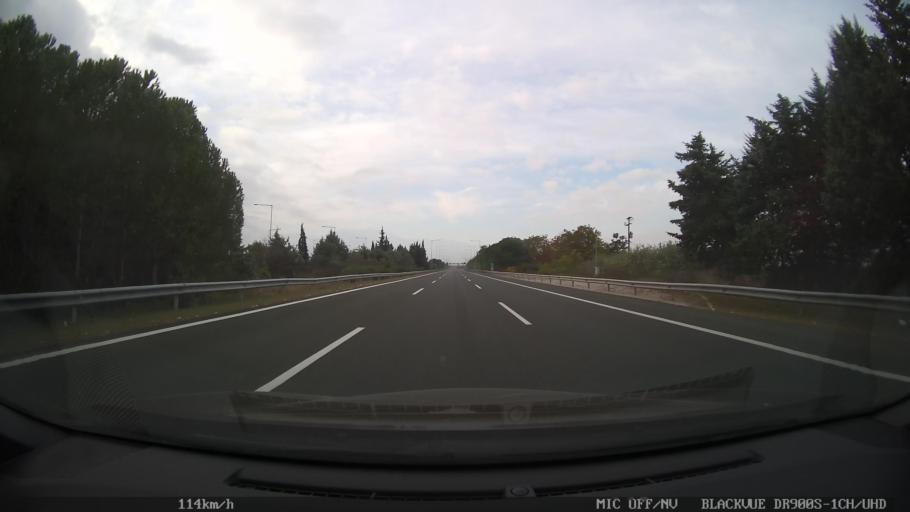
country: GR
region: Central Macedonia
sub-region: Nomos Pierias
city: Peristasi
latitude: 40.2947
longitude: 22.5411
